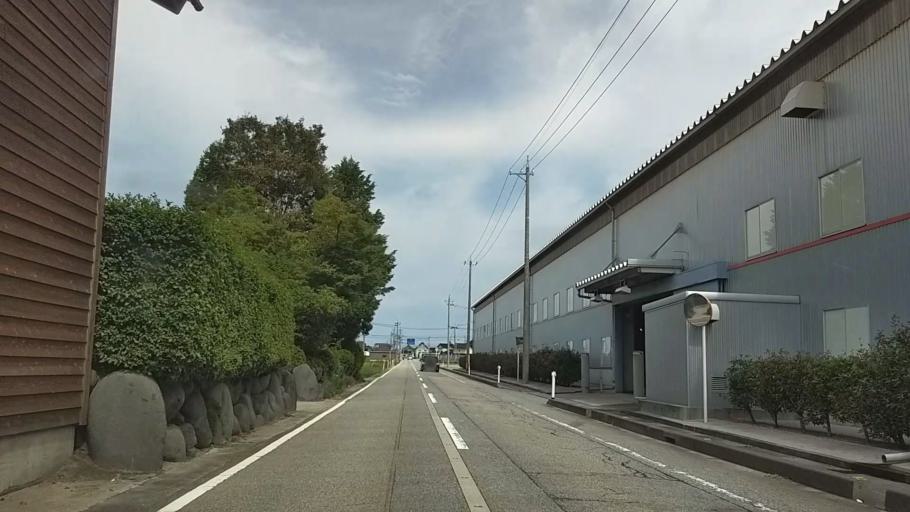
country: JP
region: Toyama
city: Kamiichi
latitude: 36.7445
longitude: 137.3735
